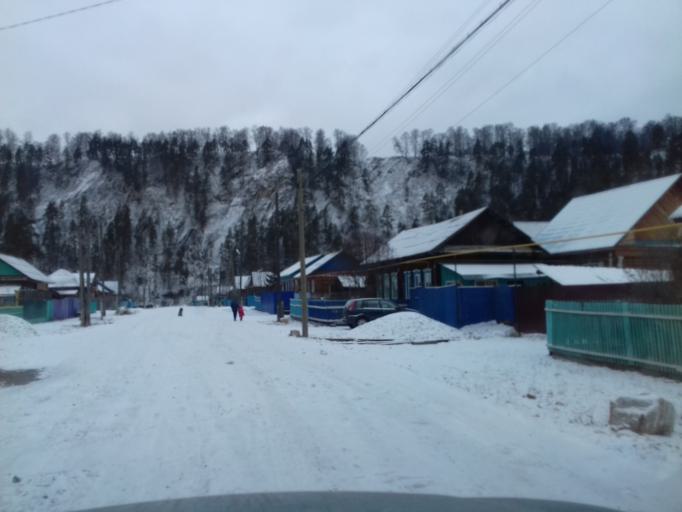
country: RU
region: Bashkortostan
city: Starosubkhangulovo
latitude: 53.0908
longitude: 57.4221
